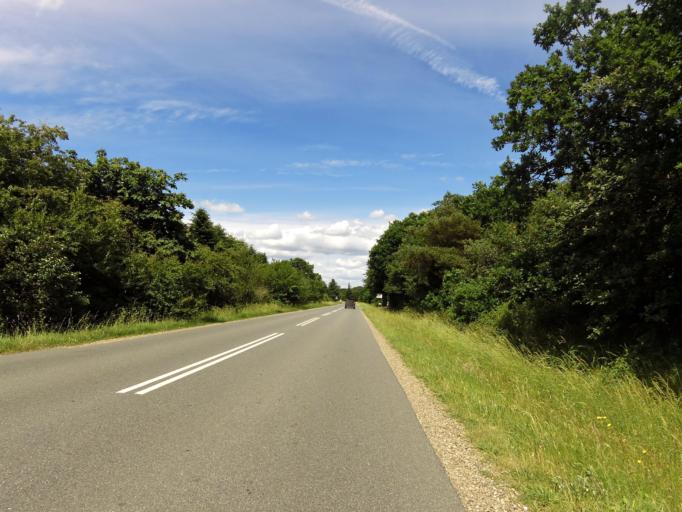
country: DK
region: South Denmark
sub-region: Esbjerg Kommune
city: Ribe
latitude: 55.3034
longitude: 8.7680
